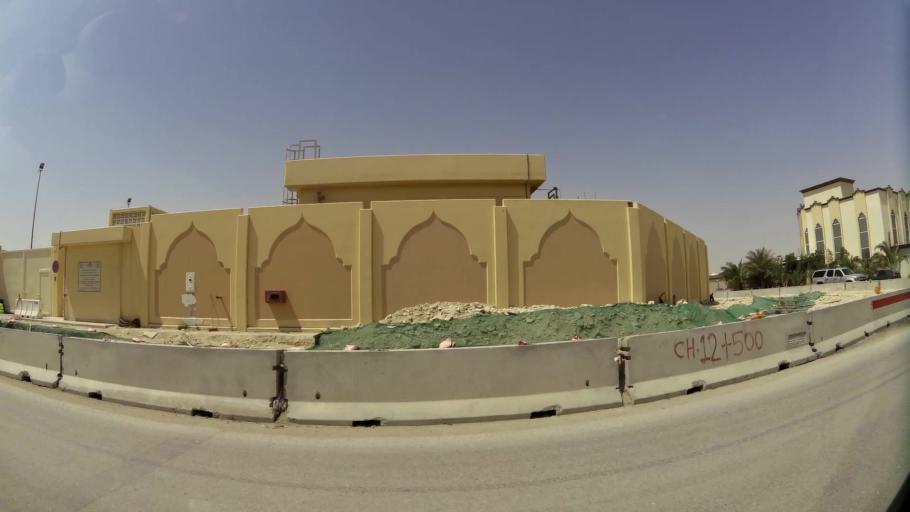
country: QA
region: Baladiyat Umm Salal
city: Umm Salal Muhammad
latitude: 25.3710
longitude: 51.4756
